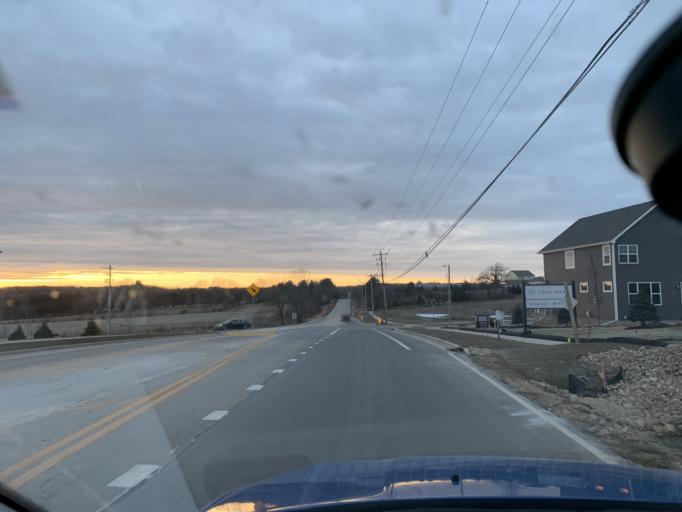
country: US
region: Wisconsin
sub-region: Dane County
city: Verona
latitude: 43.0458
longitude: -89.5563
